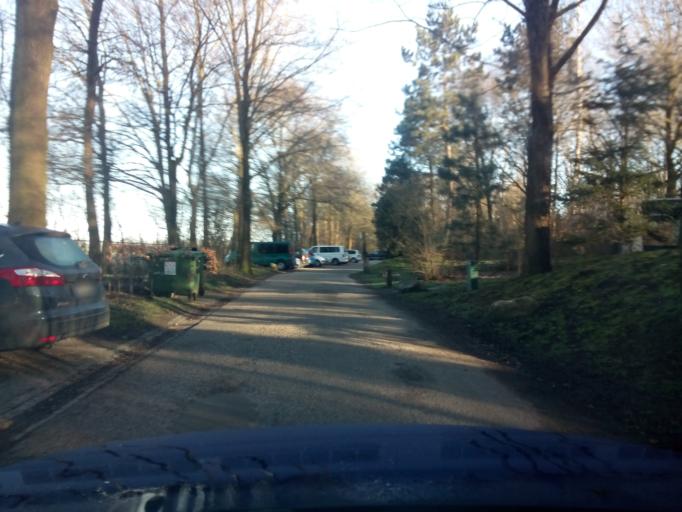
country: NL
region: Drenthe
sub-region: Gemeente Coevorden
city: Coevorden
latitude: 52.6732
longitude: 6.7639
